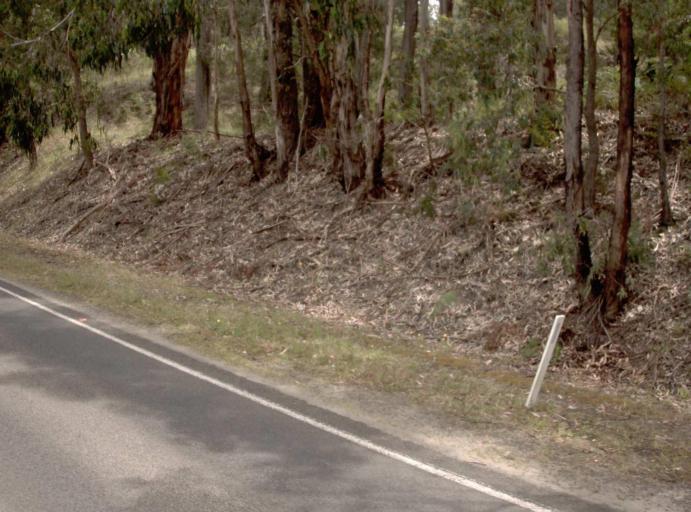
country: AU
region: Victoria
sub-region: Latrobe
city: Traralgon
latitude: -38.4604
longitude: 146.7263
